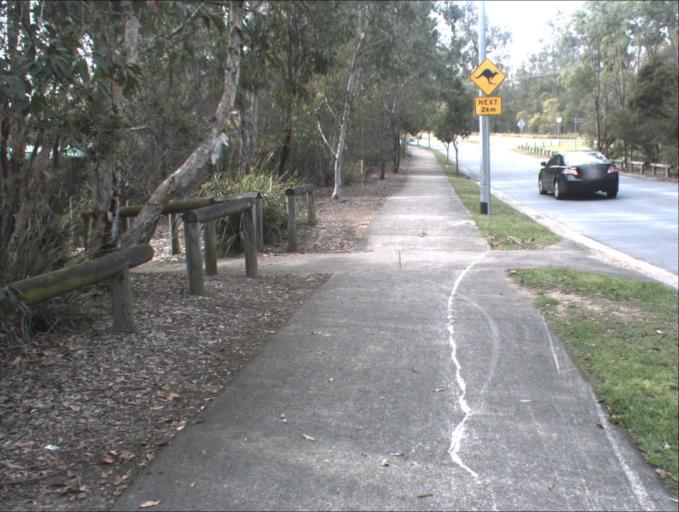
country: AU
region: Queensland
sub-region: Logan
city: Park Ridge South
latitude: -27.6904
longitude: 153.0575
